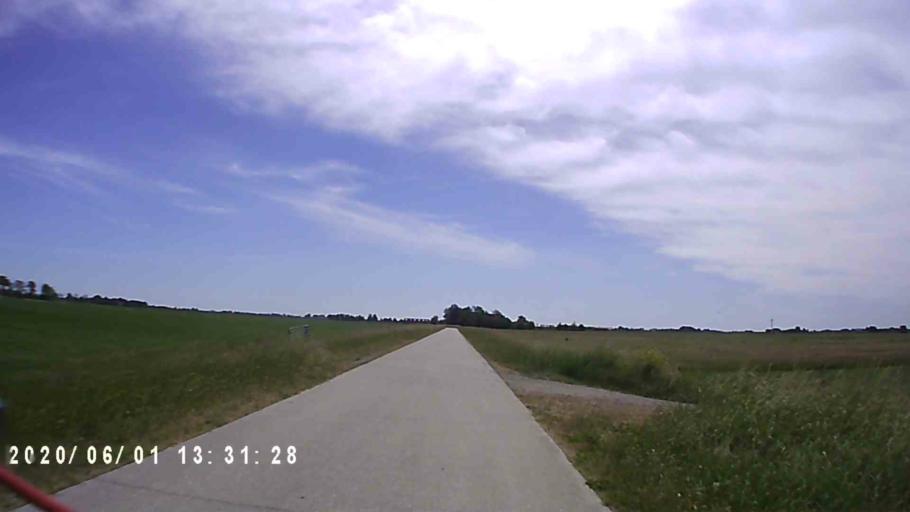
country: NL
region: Friesland
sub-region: Gemeente Littenseradiel
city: Wommels
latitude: 53.0968
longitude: 5.5668
